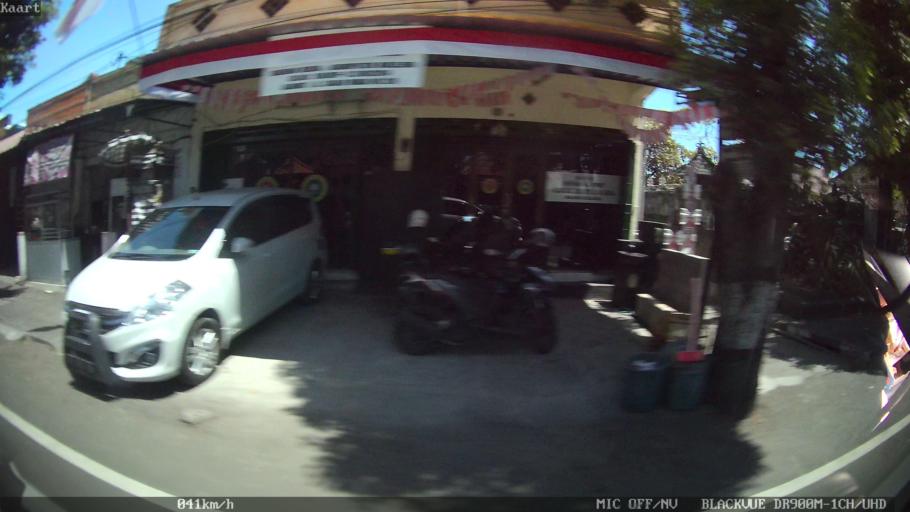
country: ID
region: Bali
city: Banjar Peguyangan
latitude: -8.1153
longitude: 115.0945
